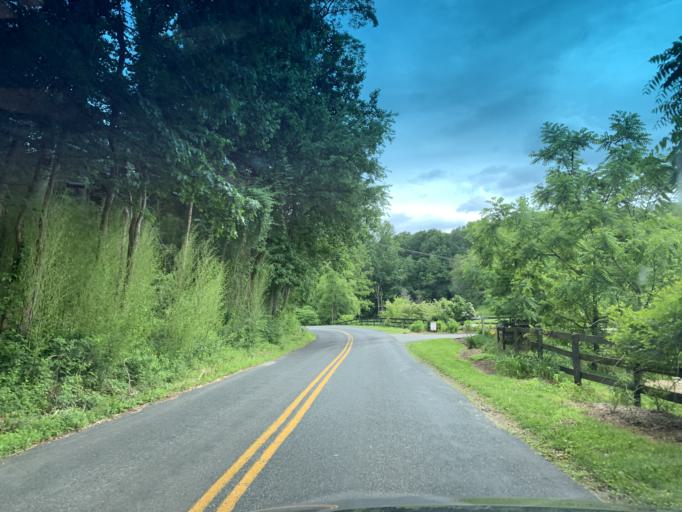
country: US
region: Maryland
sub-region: Harford County
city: Jarrettsville
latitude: 39.6245
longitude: -76.5019
